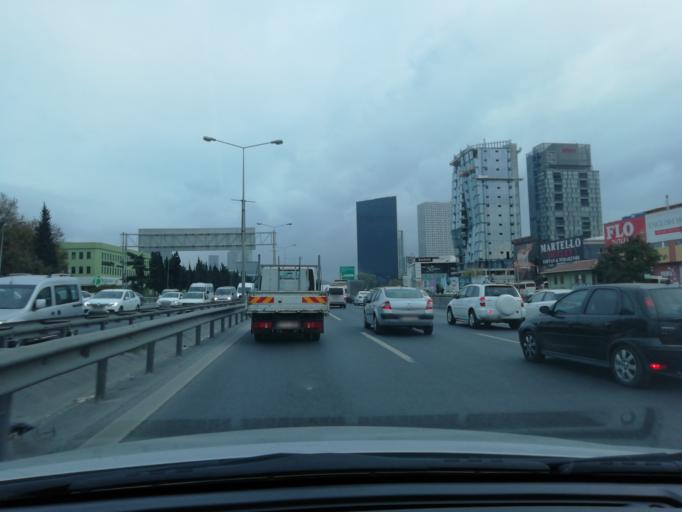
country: TR
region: Istanbul
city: Mahmutbey
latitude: 41.0491
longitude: 28.8083
